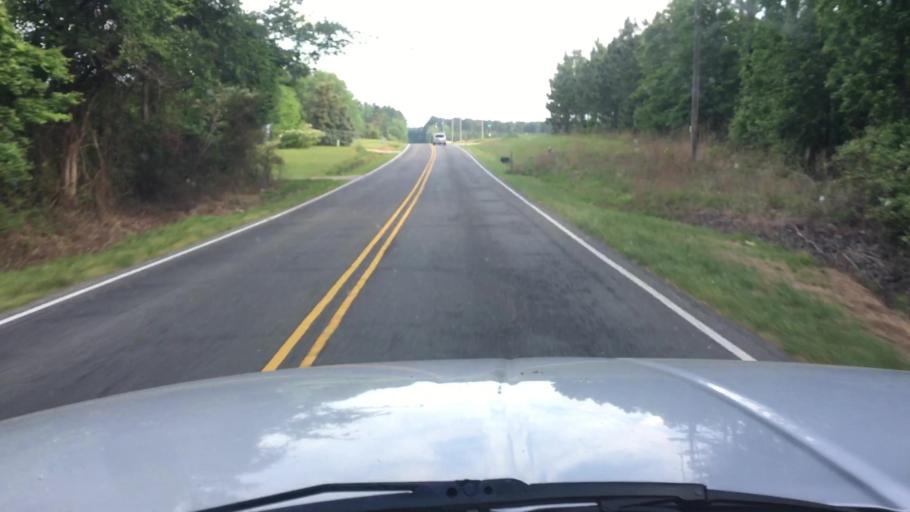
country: US
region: North Carolina
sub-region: Johnston County
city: Wilsons Mills
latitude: 35.6220
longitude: -78.3271
